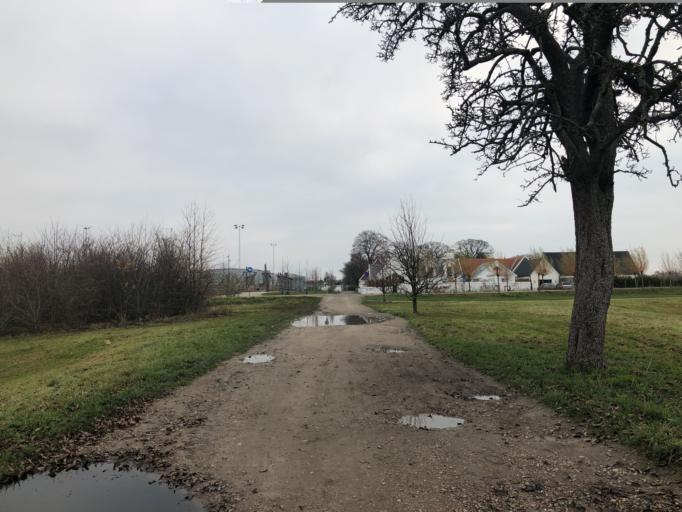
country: SE
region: Skane
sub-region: Malmo
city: Tygelsjo
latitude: 55.5201
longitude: 12.9906
